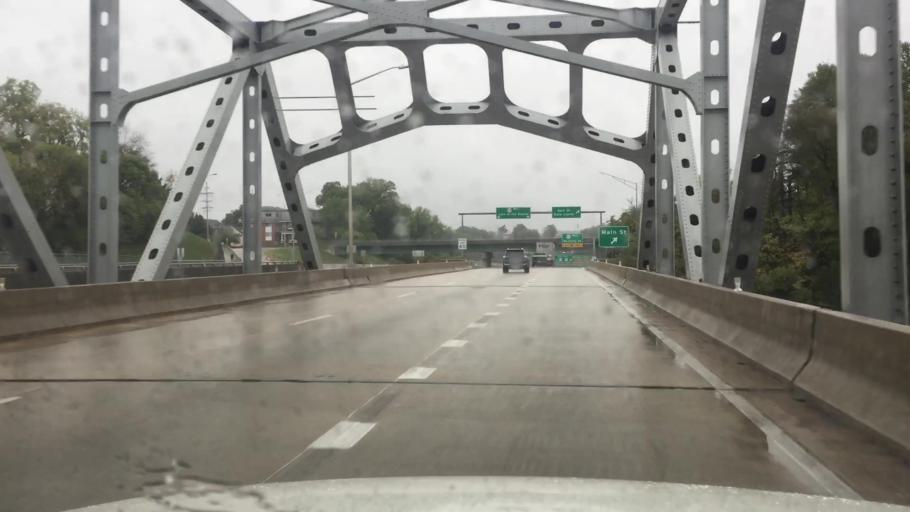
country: US
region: Missouri
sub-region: Cole County
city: Jefferson City
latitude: 38.5867
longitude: -92.1798
